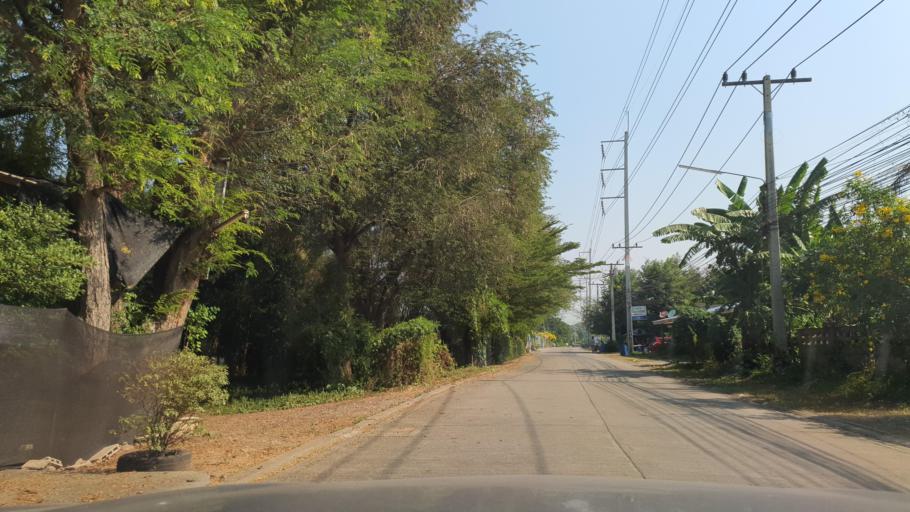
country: TH
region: Kanchanaburi
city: Kanchanaburi
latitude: 14.0630
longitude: 99.4855
